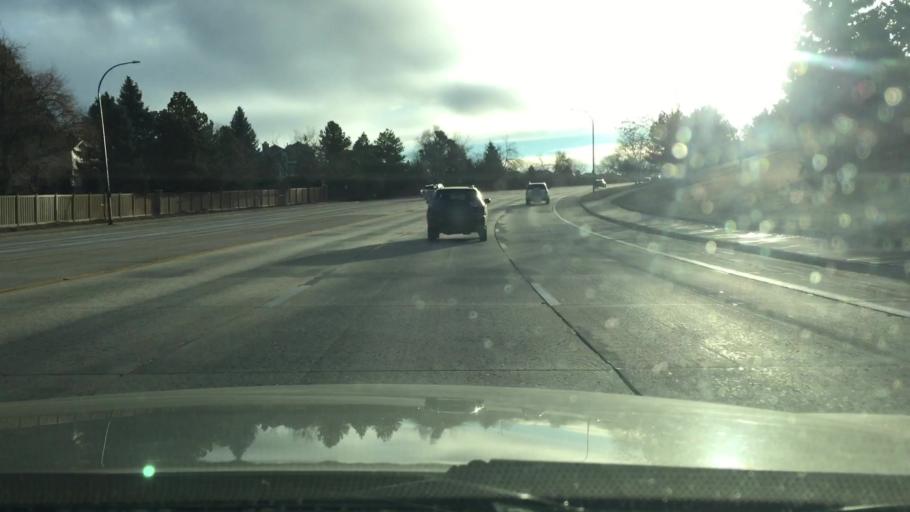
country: US
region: Colorado
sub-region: Douglas County
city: Highlands Ranch
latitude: 39.5462
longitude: -104.9767
